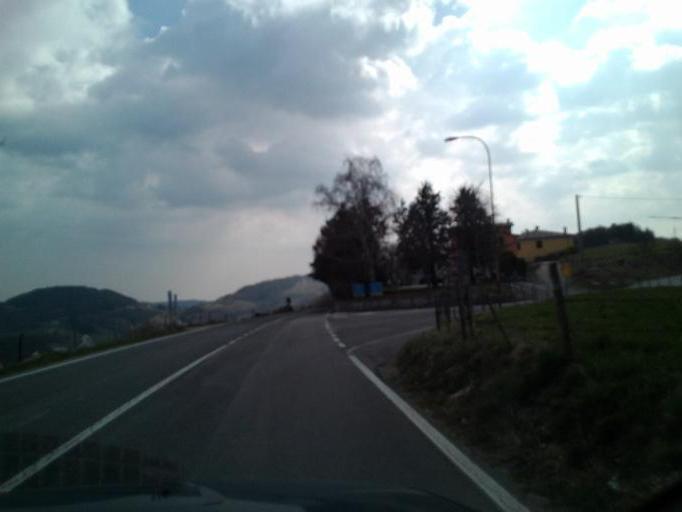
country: IT
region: Veneto
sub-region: Provincia di Verona
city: Sant'Anna d'Alfaedo
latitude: 45.6182
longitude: 10.9489
